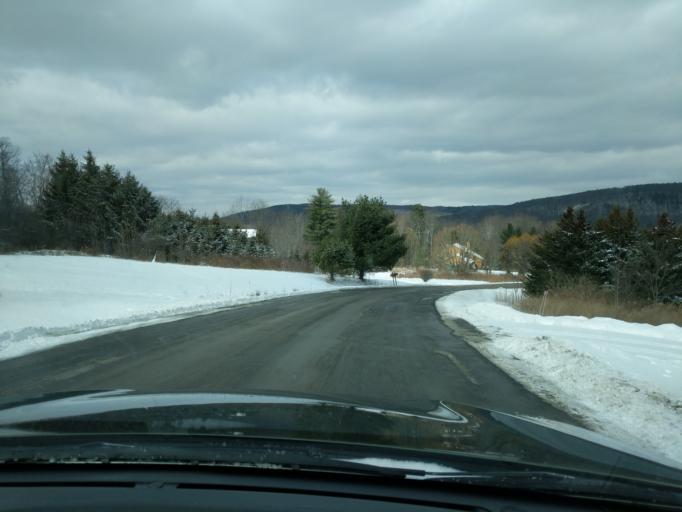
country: US
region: New York
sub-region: Tompkins County
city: Northeast Ithaca
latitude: 42.4279
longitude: -76.4001
